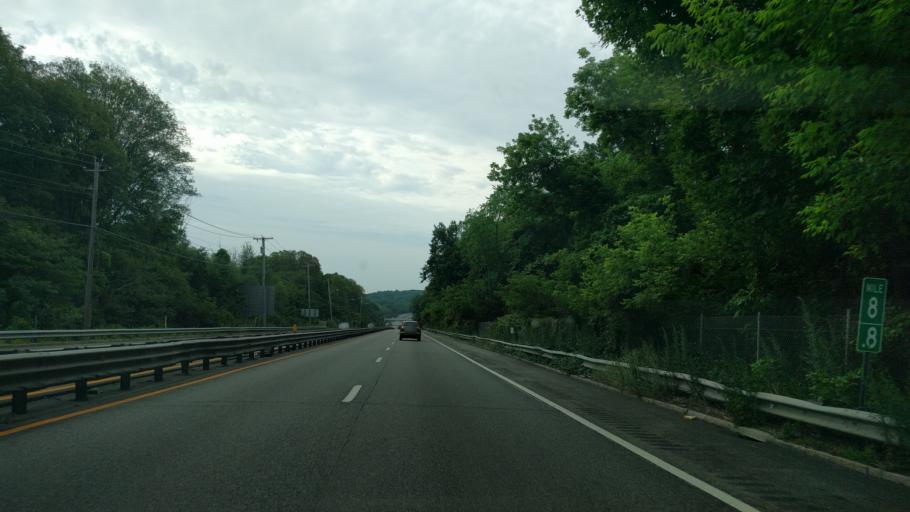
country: US
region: Rhode Island
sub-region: Providence County
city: Cumberland Hill
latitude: 41.9316
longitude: -71.4633
